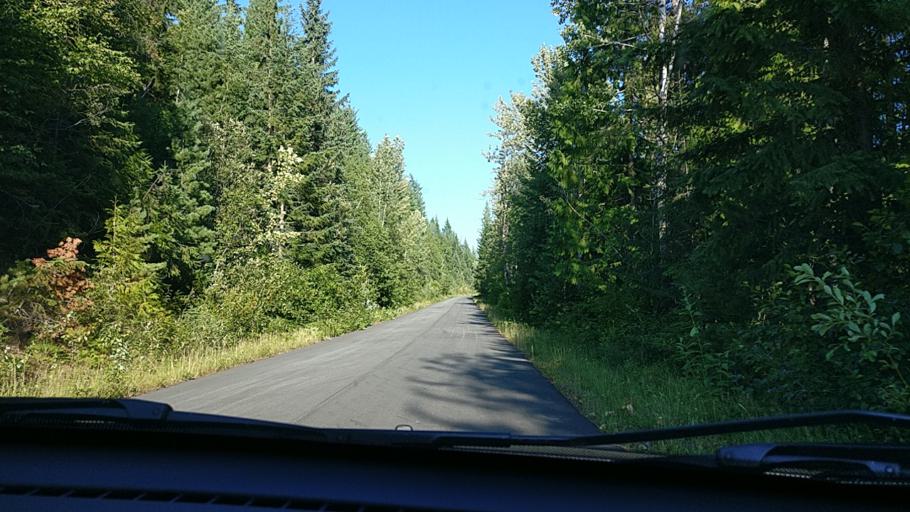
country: CA
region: British Columbia
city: Revelstoke
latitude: 51.0080
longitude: -118.1800
